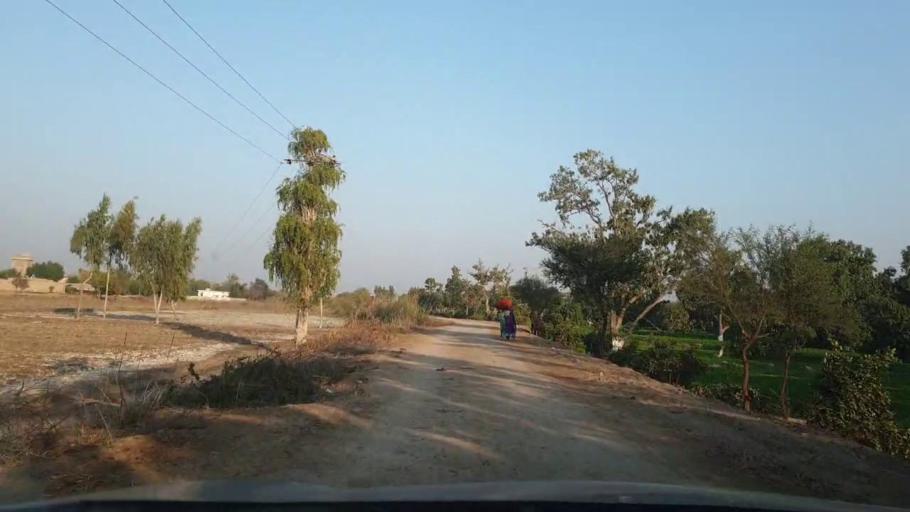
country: PK
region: Sindh
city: Tando Allahyar
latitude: 25.5463
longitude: 68.8524
